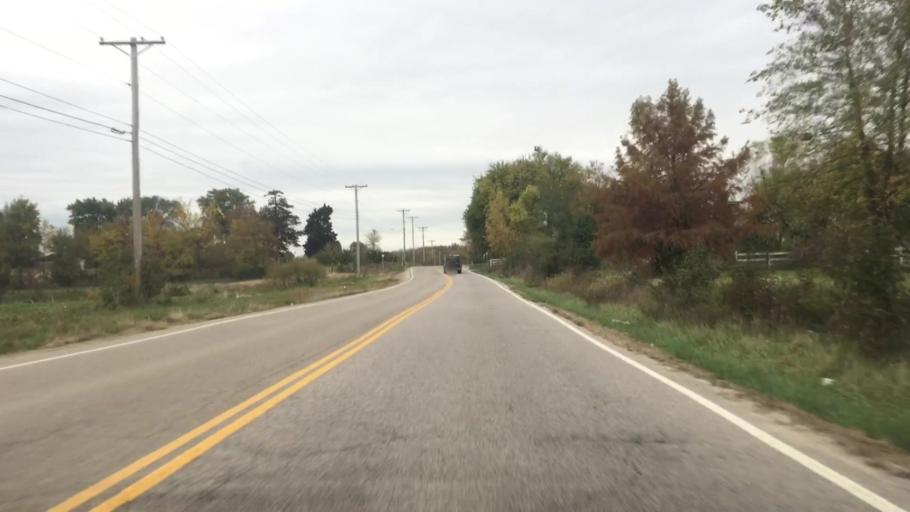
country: US
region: Missouri
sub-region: Jackson County
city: Lees Summit
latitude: 38.8893
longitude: -94.3593
